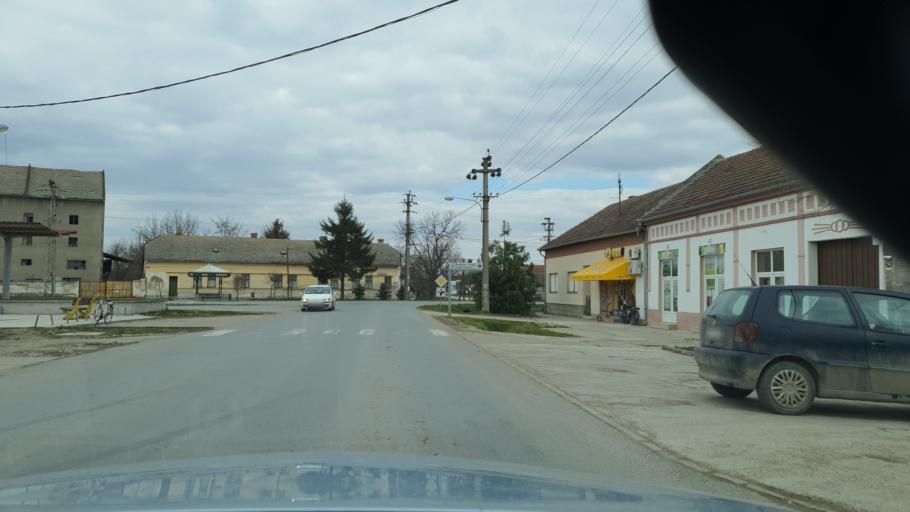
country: RS
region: Autonomna Pokrajina Vojvodina
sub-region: Juznobacki Okrug
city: Bac
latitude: 45.3946
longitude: 19.2372
